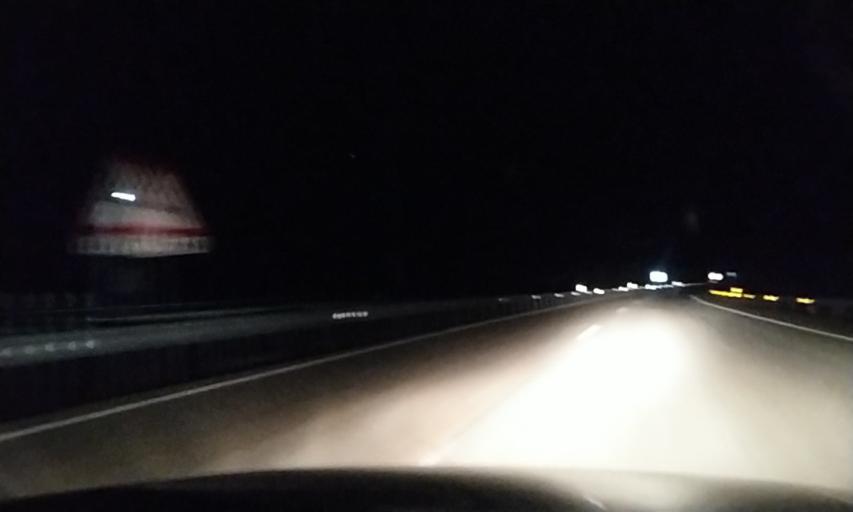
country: ES
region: Castille and Leon
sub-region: Provincia de Zamora
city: Requejo
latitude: 42.0335
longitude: -6.7483
